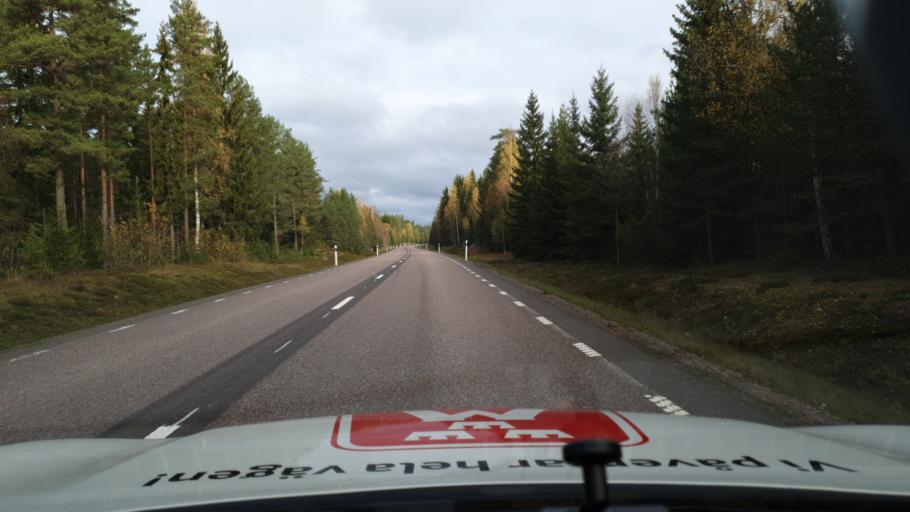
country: SE
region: Gaevleborg
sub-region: Gavle Kommun
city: Hedesunda
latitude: 60.3668
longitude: 16.9684
